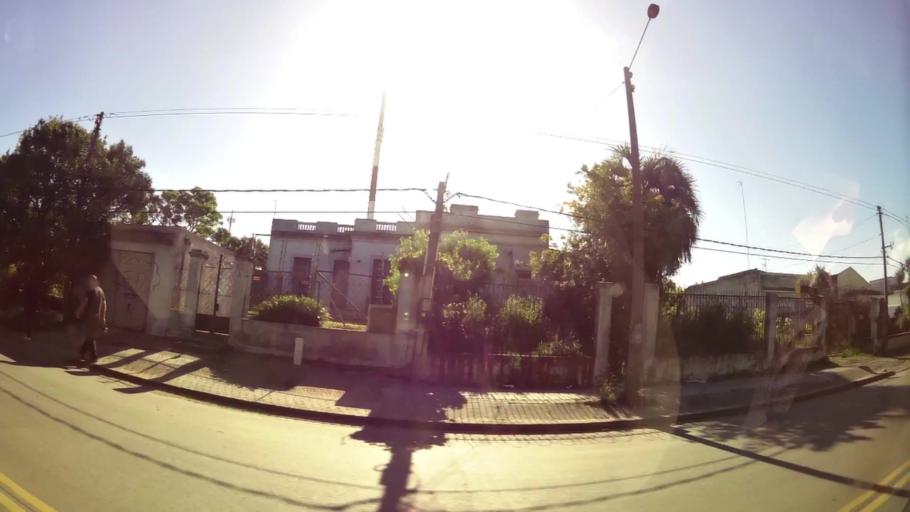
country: UY
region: Montevideo
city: Montevideo
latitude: -34.8272
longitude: -56.1548
